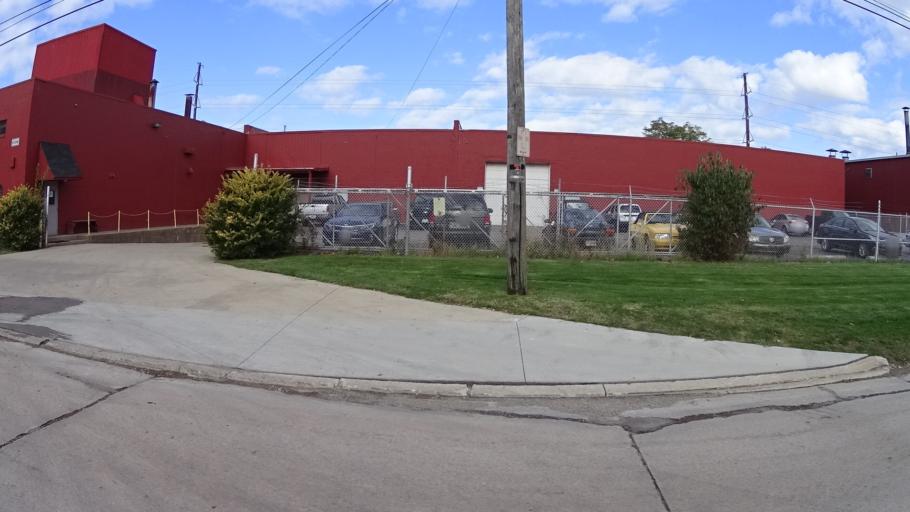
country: US
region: Ohio
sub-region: Lorain County
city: Sheffield
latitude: 41.4458
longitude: -82.1138
